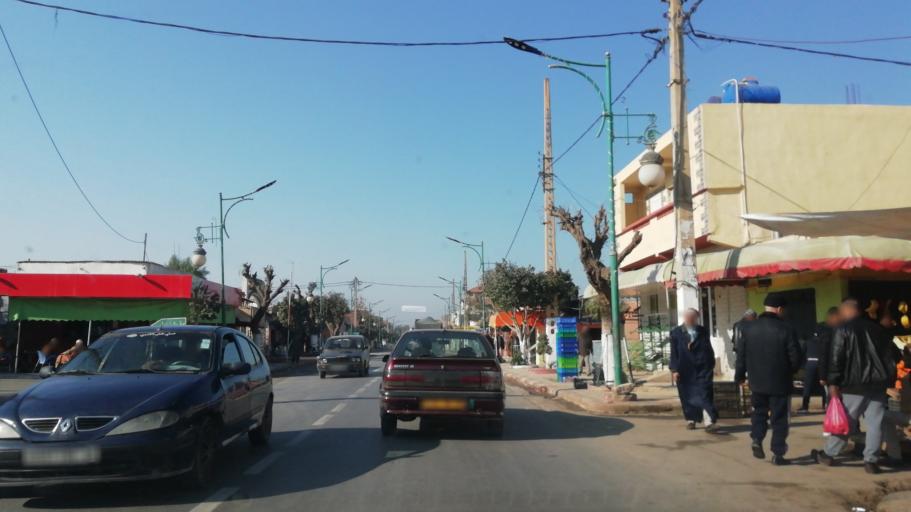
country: DZ
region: Relizane
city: Relizane
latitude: 35.7338
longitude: 0.4601
